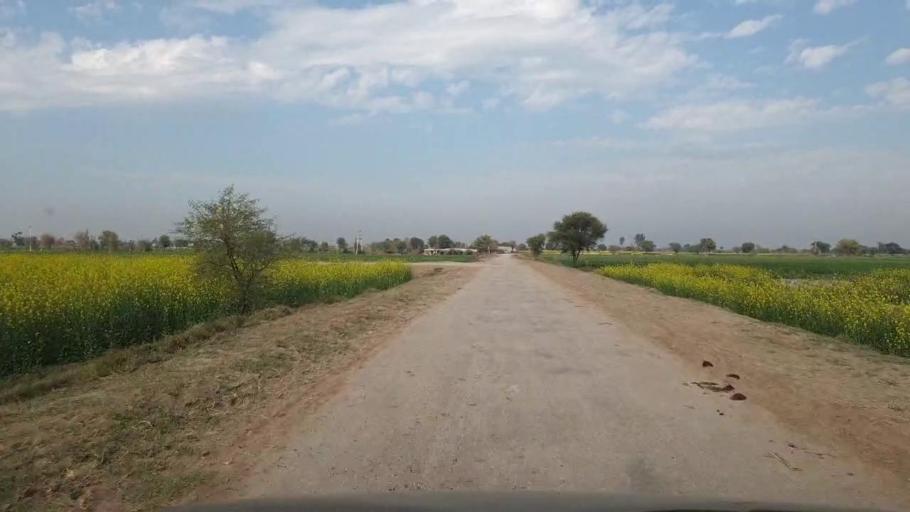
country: PK
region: Sindh
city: Hala
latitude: 26.0057
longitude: 68.4151
